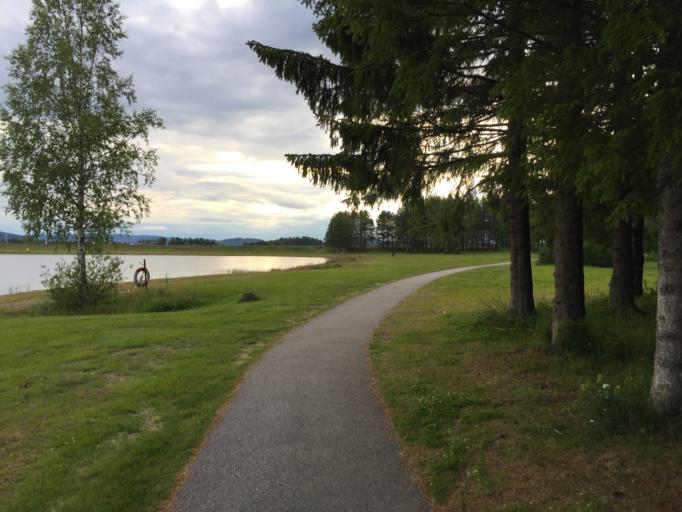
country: SE
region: Vaesterbotten
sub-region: Storumans Kommun
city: Storuman
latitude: 65.1029
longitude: 17.1177
